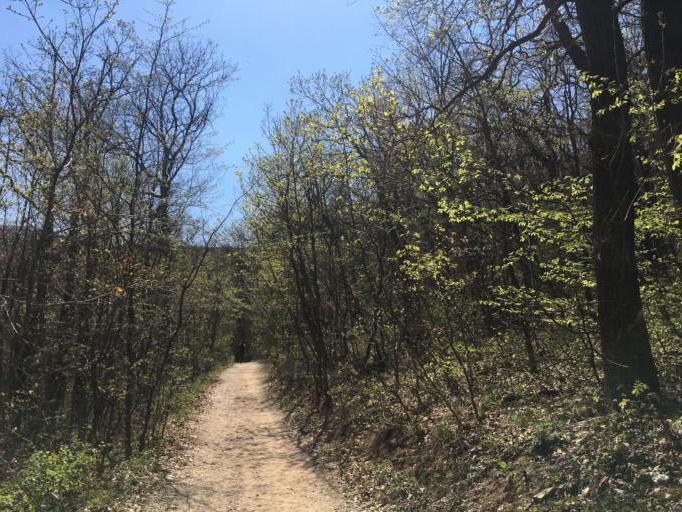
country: XK
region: Pristina
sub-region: Komuna e Prishtines
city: Pristina
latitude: 42.6650
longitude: 21.2195
